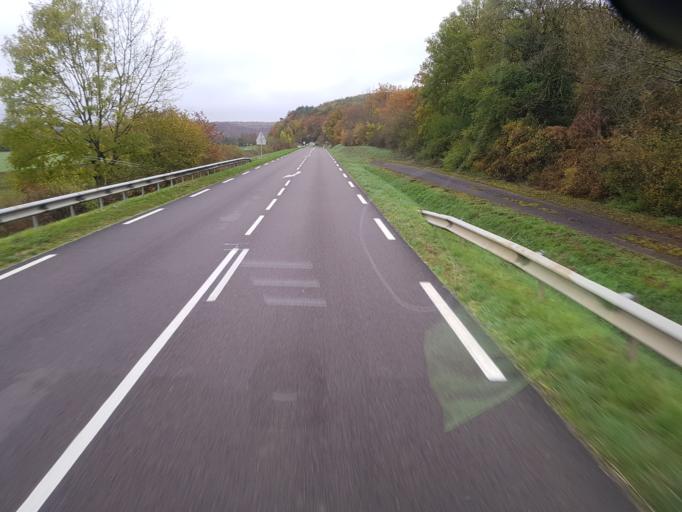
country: FR
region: Bourgogne
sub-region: Departement de la Cote-d'Or
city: Is-sur-Tille
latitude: 47.5290
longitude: 4.9944
